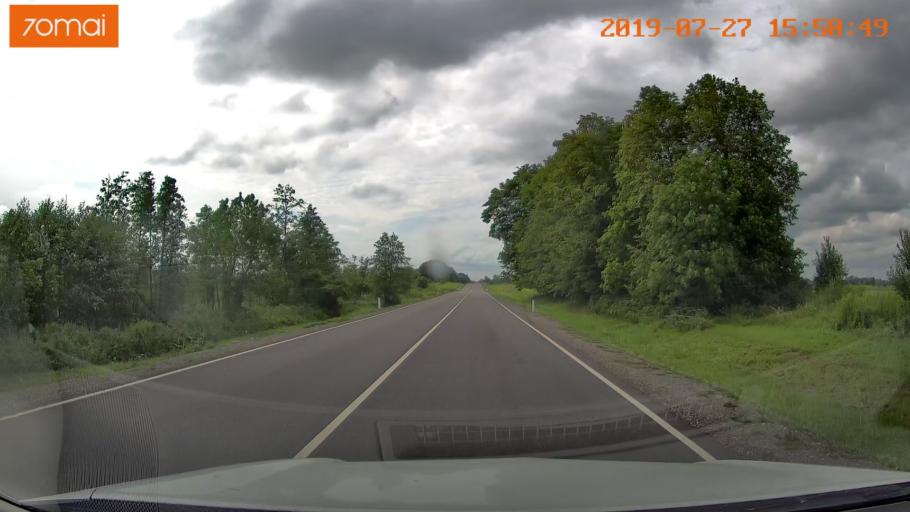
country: RU
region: Kaliningrad
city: Chernyakhovsk
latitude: 54.6017
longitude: 21.9970
